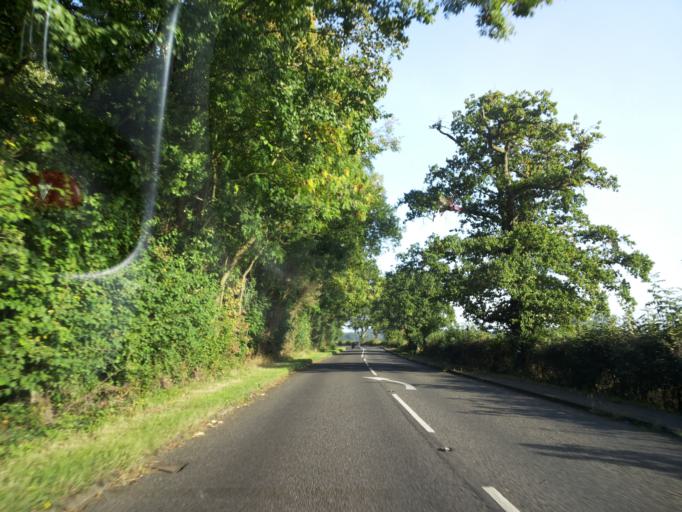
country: GB
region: England
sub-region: Warwickshire
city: Wroxall
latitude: 52.3315
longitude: -1.6670
